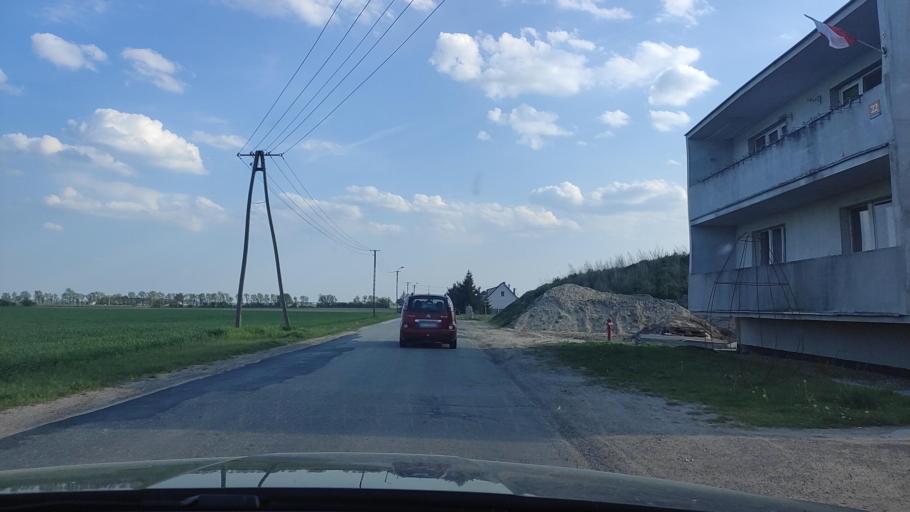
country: PL
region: Greater Poland Voivodeship
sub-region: Powiat poznanski
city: Kleszczewo
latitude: 52.3766
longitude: 17.1668
